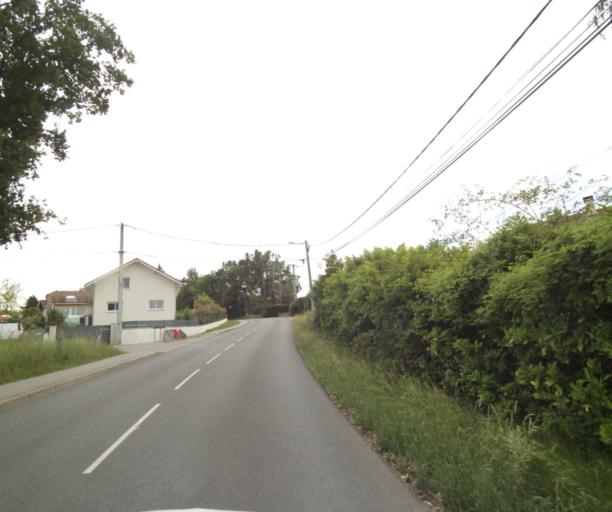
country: FR
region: Rhone-Alpes
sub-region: Departement de la Haute-Savoie
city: Sciez
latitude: 46.3306
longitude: 6.3910
